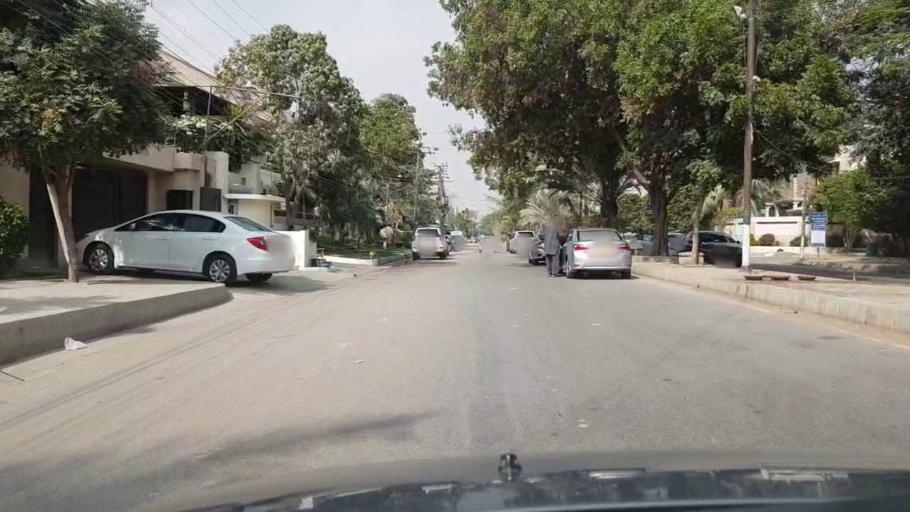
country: PK
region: Sindh
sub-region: Karachi District
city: Karachi
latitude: 24.8726
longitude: 67.0878
